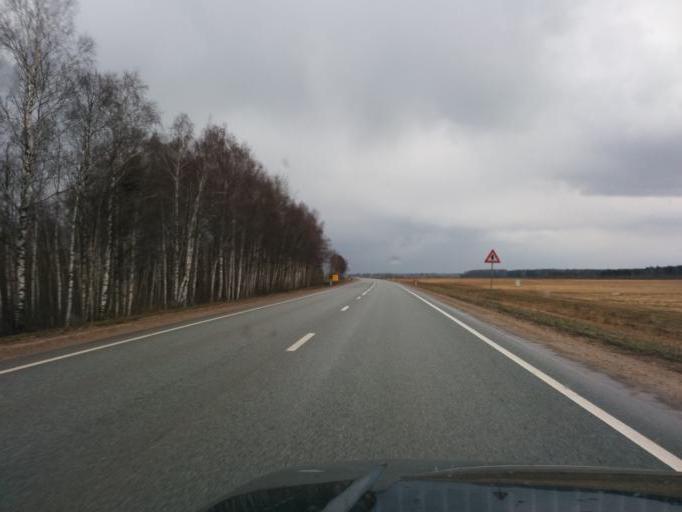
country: LV
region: Marupe
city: Marupe
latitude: 56.8545
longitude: 24.0006
